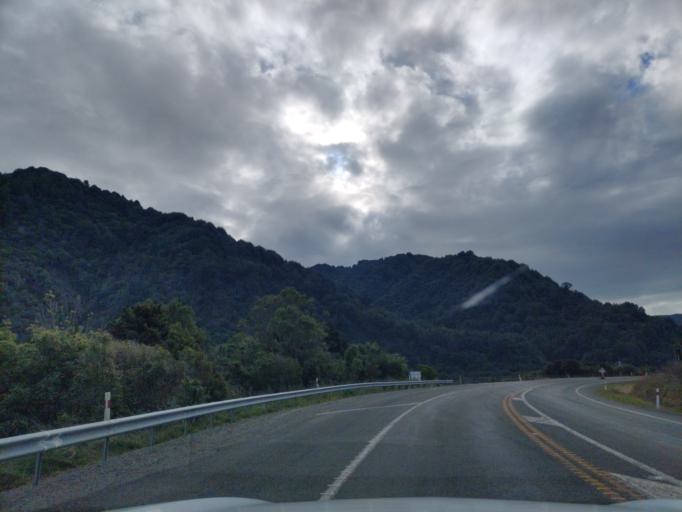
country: NZ
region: Manawatu-Wanganui
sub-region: Palmerston North City
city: Palmerston North
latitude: -40.3355
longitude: 175.8176
